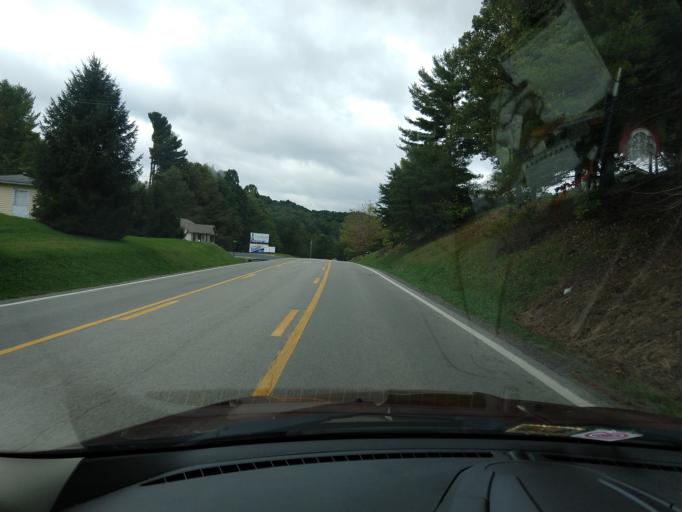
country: US
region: West Virginia
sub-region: Barbour County
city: Philippi
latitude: 39.1298
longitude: -80.0030
